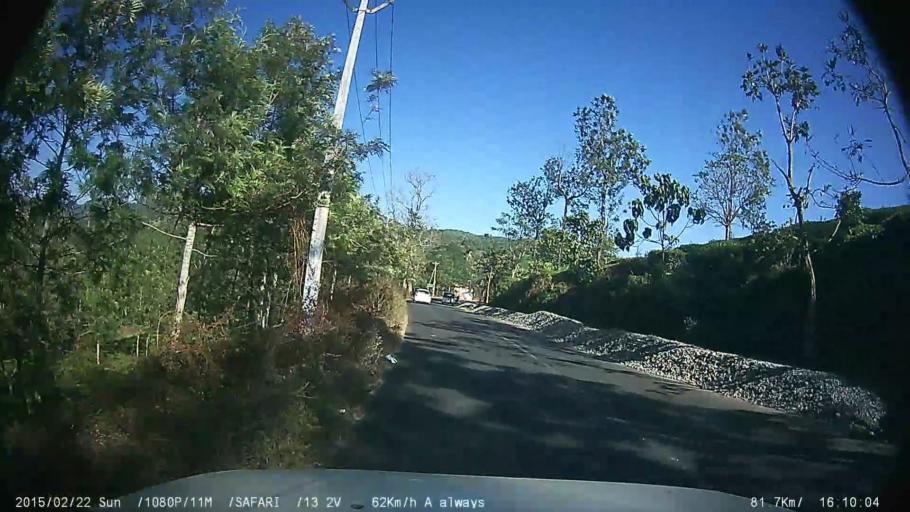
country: IN
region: Tamil Nadu
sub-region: Theni
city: Gudalur
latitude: 9.5709
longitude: 77.0844
